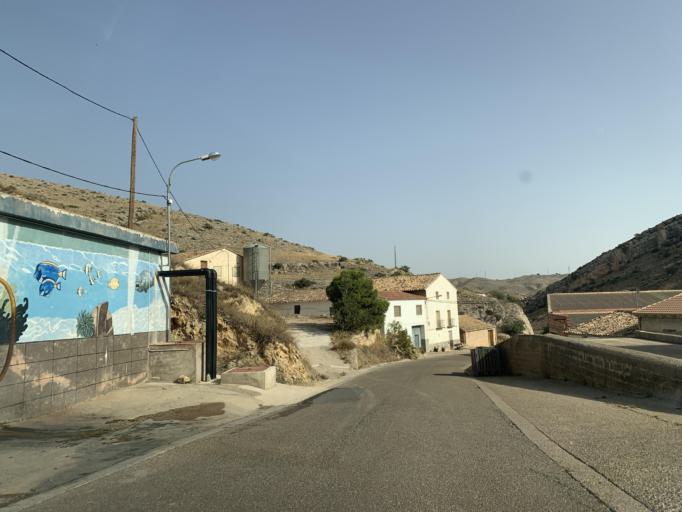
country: ES
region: Aragon
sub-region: Provincia de Zaragoza
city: Almonacid de la Cuba
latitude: 41.2754
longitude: -0.7907
